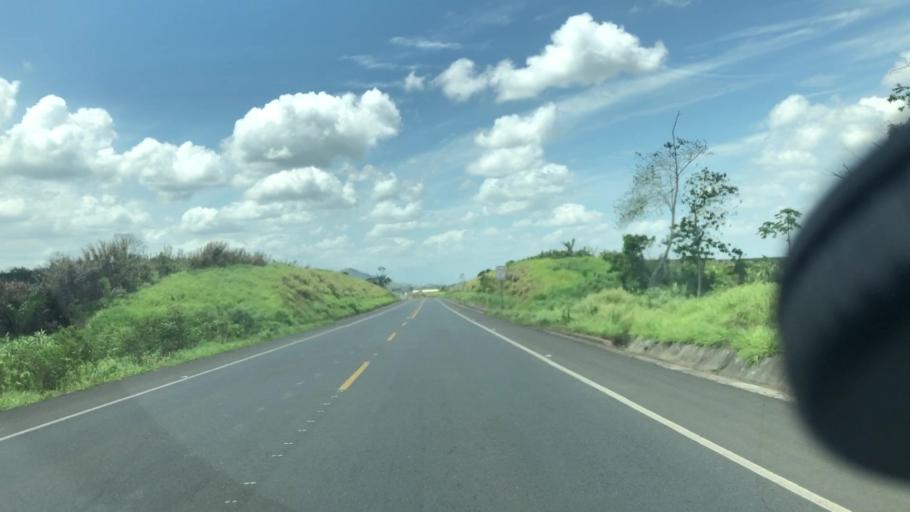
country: CR
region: Alajuela
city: Pital
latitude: 10.4346
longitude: -84.2857
